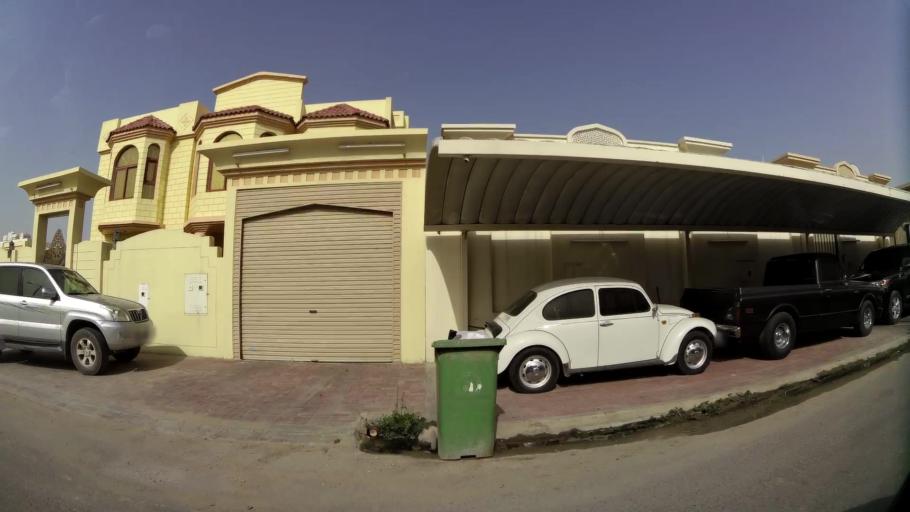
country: QA
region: Baladiyat ar Rayyan
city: Ar Rayyan
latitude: 25.2435
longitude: 51.4469
